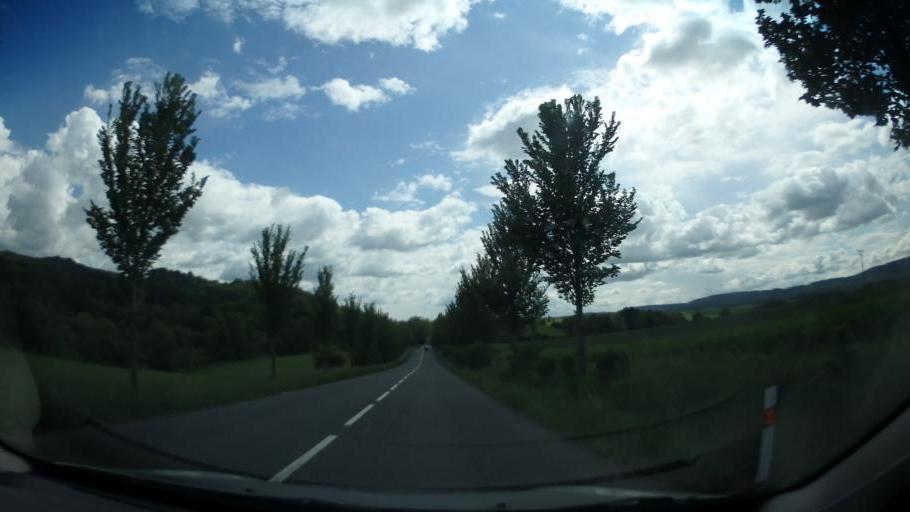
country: CZ
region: Pardubicky
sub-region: Okres Svitavy
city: Moravska Trebova
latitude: 49.7228
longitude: 16.6404
